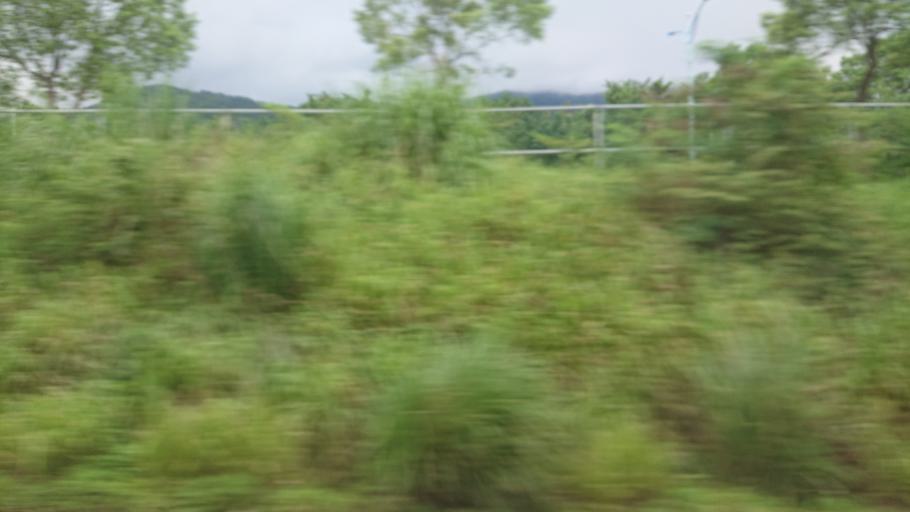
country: TW
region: Taiwan
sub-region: Hualien
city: Hualian
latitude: 23.8250
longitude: 121.4791
